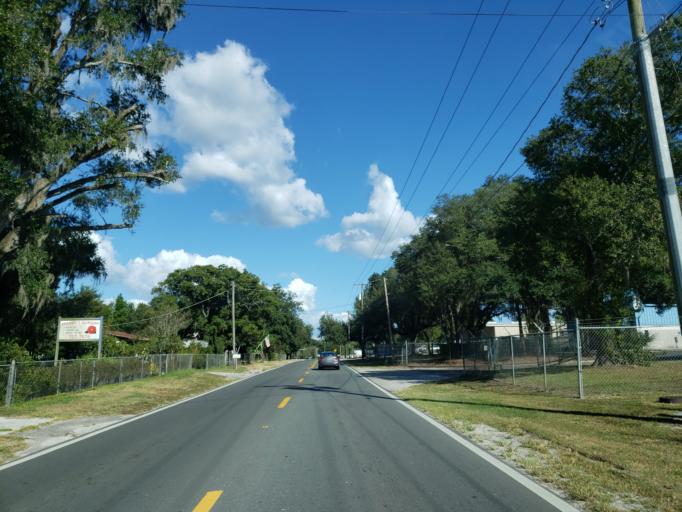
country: US
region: Florida
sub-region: Hillsborough County
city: Plant City
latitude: 28.0034
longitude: -82.1521
